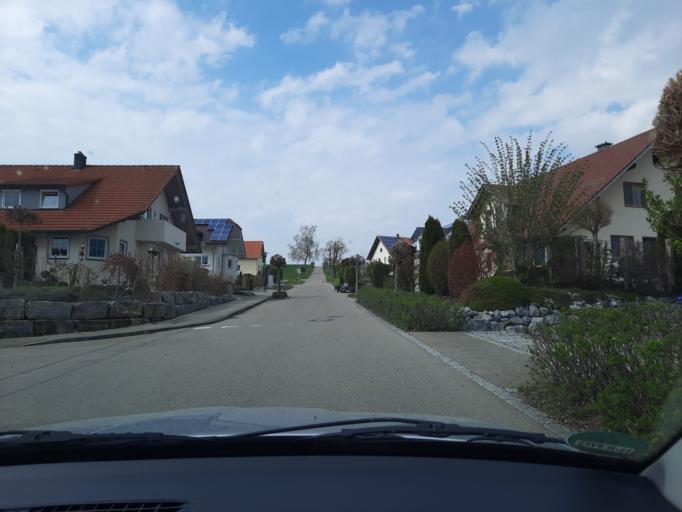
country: DE
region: Baden-Wuerttemberg
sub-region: Tuebingen Region
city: Steinhausen an der Rottum
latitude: 47.9802
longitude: 9.9402
